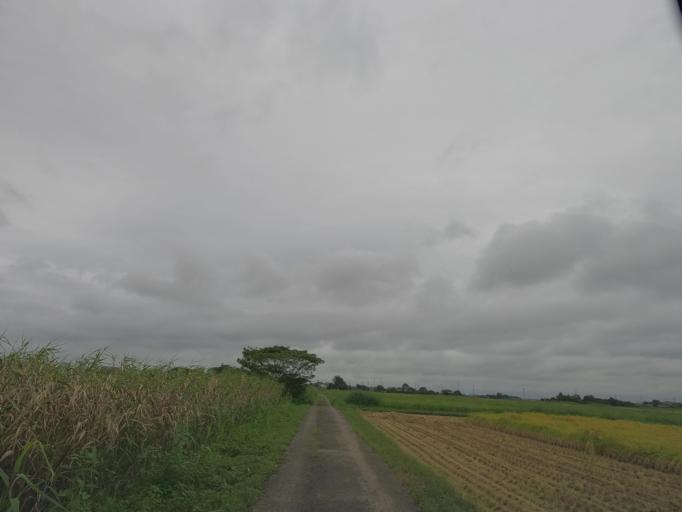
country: JP
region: Ibaraki
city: Toride
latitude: 35.9259
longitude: 140.0685
